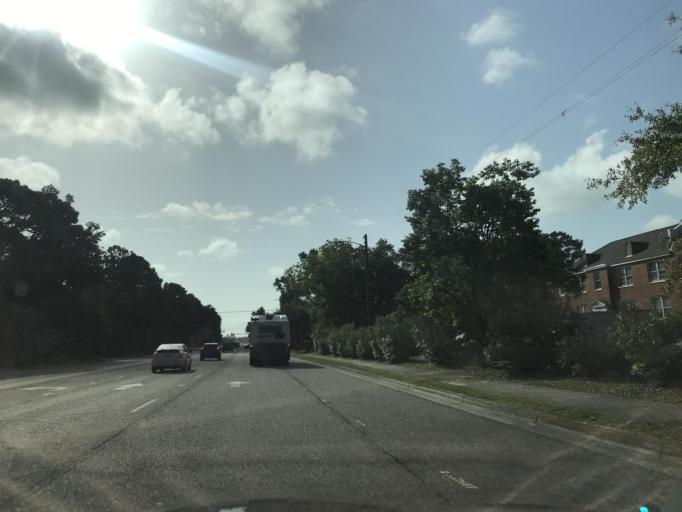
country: US
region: North Carolina
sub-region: New Hanover County
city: Wilmington
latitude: 34.2185
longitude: -77.9095
